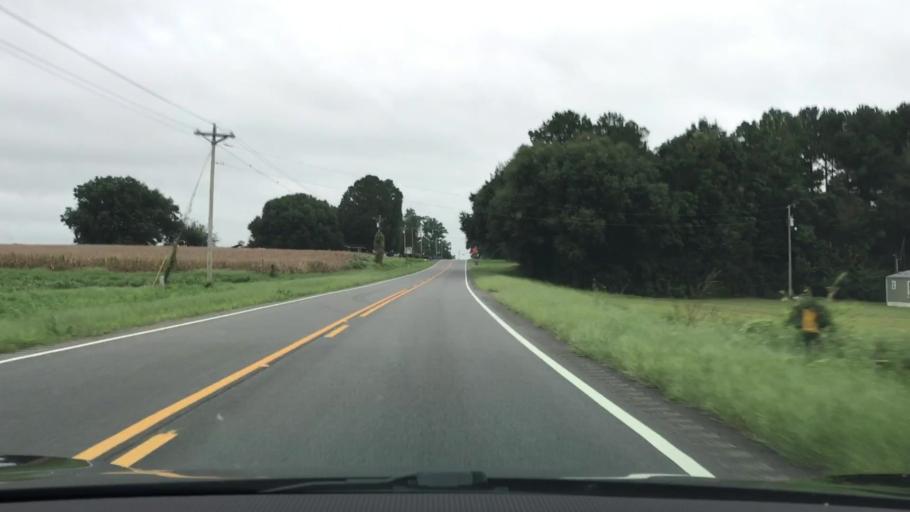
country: US
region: Alabama
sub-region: Covington County
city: Opp
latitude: 31.2760
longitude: -86.1582
